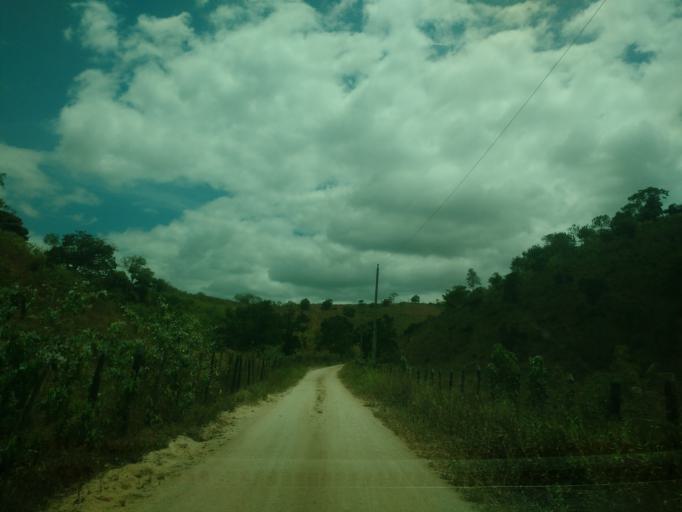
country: BR
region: Alagoas
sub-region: Santana Do Mundau
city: Santana do Mundau
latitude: -9.1507
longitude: -36.1693
